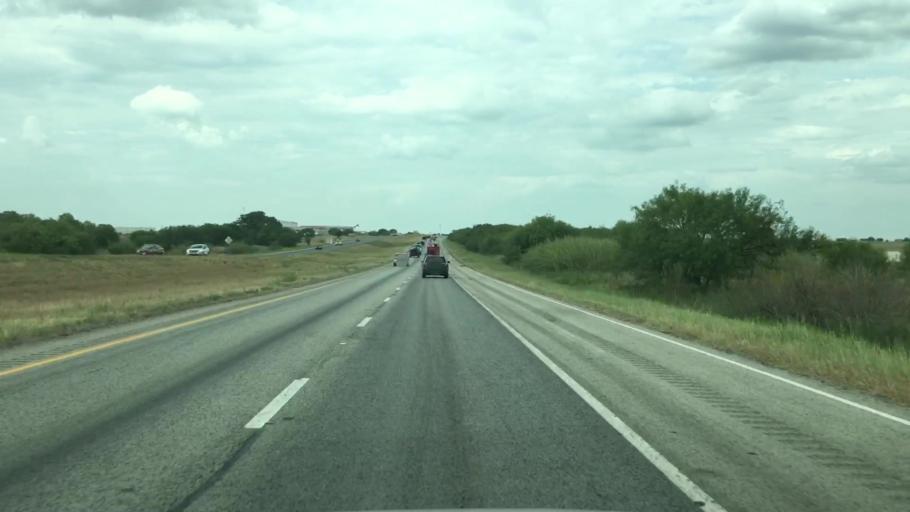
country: US
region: Texas
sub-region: Atascosa County
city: Pleasanton
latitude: 29.0885
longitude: -98.4328
